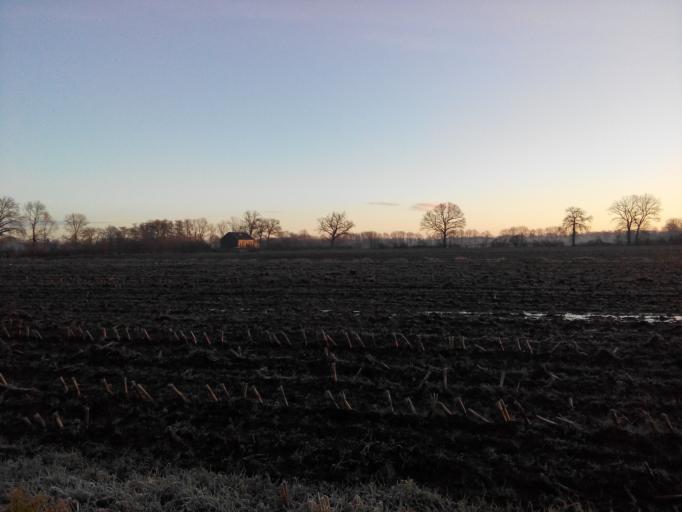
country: NL
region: Utrecht
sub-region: Gemeente Woudenberg
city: Woudenberg
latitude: 52.1054
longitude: 5.3953
